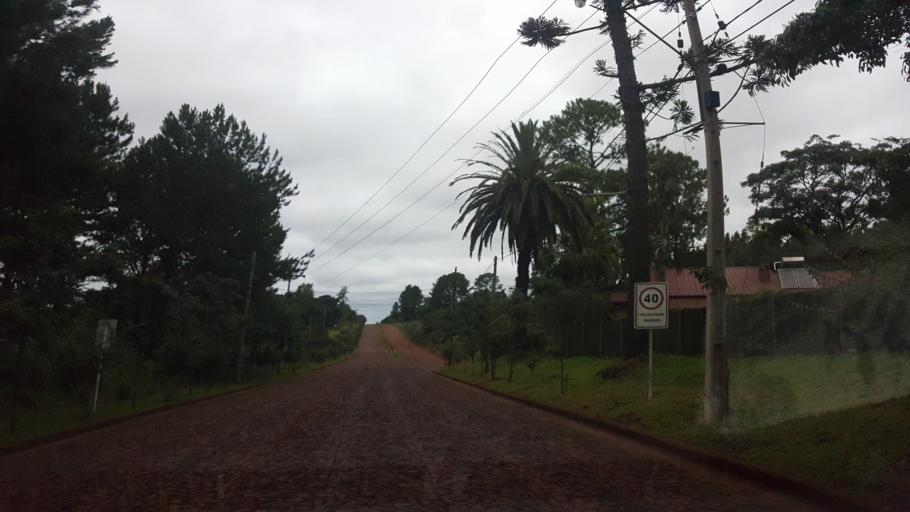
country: AR
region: Misiones
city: Ruiz de Montoya
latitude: -26.9612
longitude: -55.0564
